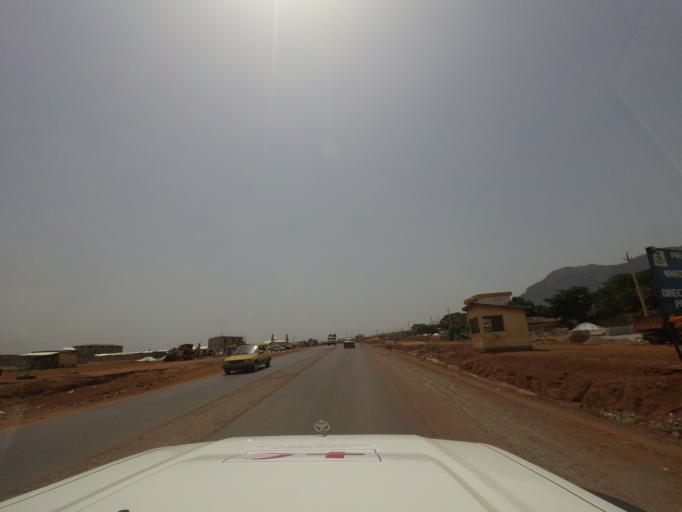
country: GN
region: Kindia
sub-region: Coyah
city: Coyah
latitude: 9.7302
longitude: -13.4291
